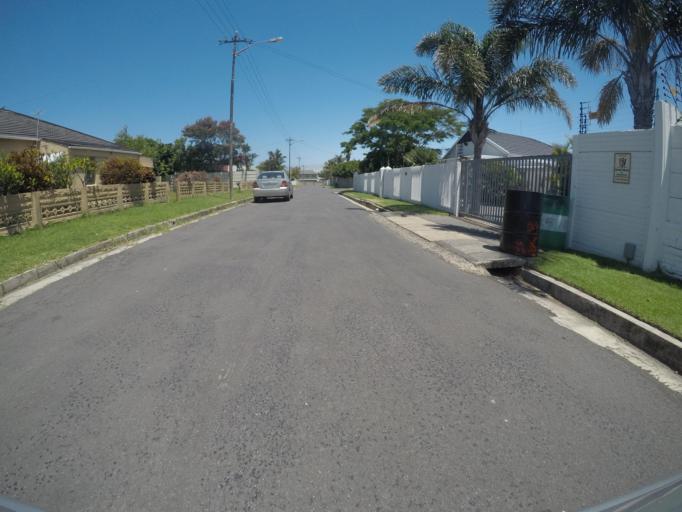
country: ZA
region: Eastern Cape
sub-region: Buffalo City Metropolitan Municipality
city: East London
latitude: -32.9865
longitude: 27.9040
